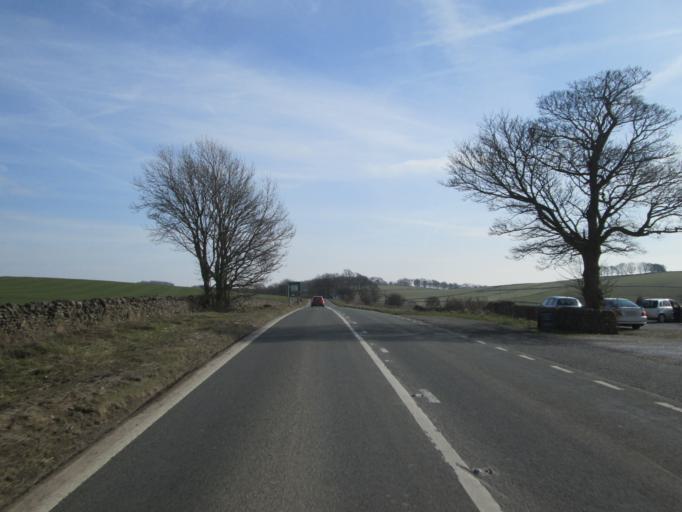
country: GB
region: England
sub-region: Derbyshire
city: Bakewell
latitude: 53.1499
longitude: -1.7667
